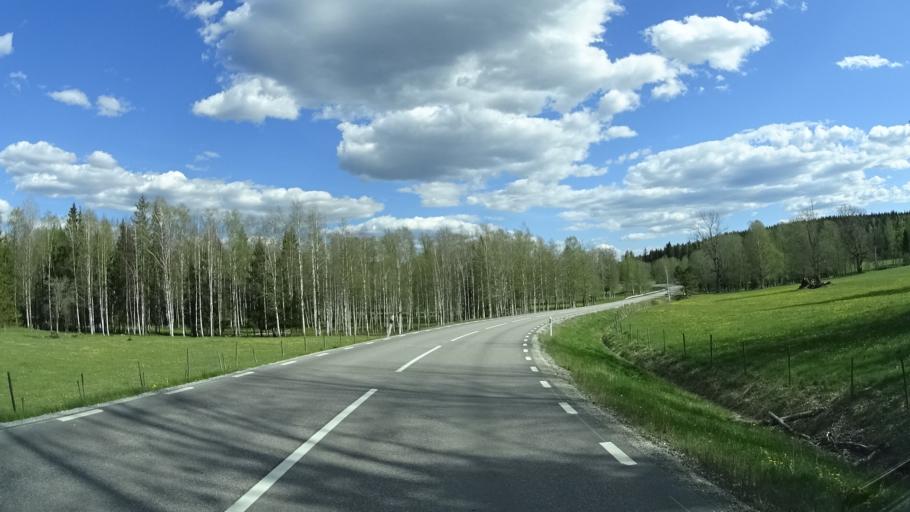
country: SE
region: OErebro
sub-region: Nora Kommun
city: As
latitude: 59.4629
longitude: 14.8653
